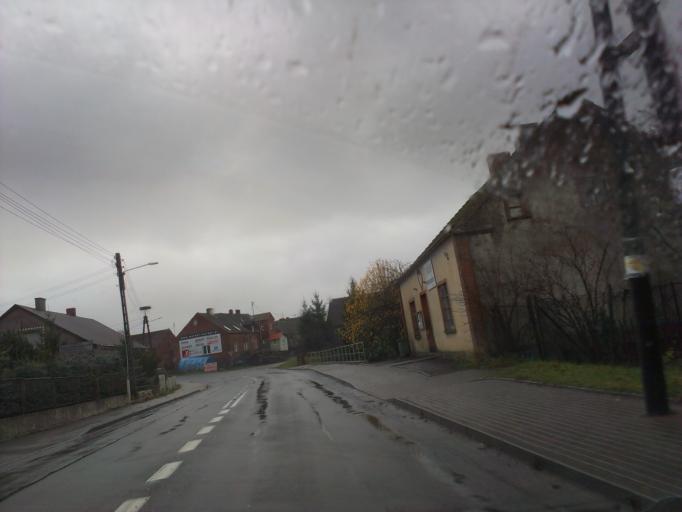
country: PL
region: West Pomeranian Voivodeship
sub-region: Powiat szczecinecki
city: Szczecinek
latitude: 53.6509
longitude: 16.6320
